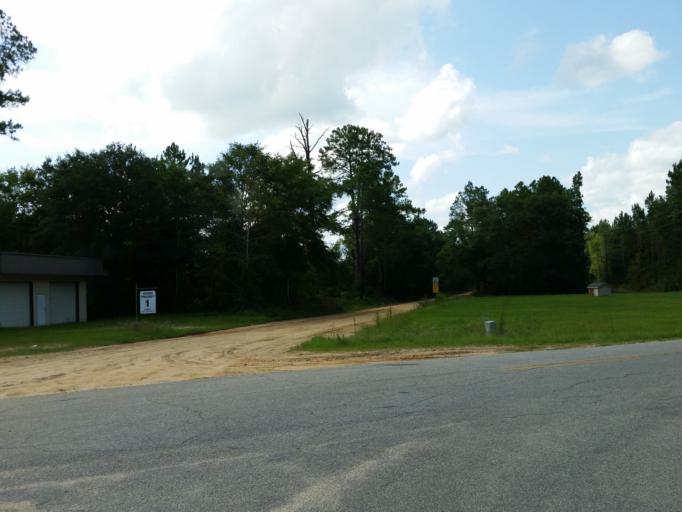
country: US
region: Georgia
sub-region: Lee County
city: Leesburg
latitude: 31.7864
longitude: -84.0540
